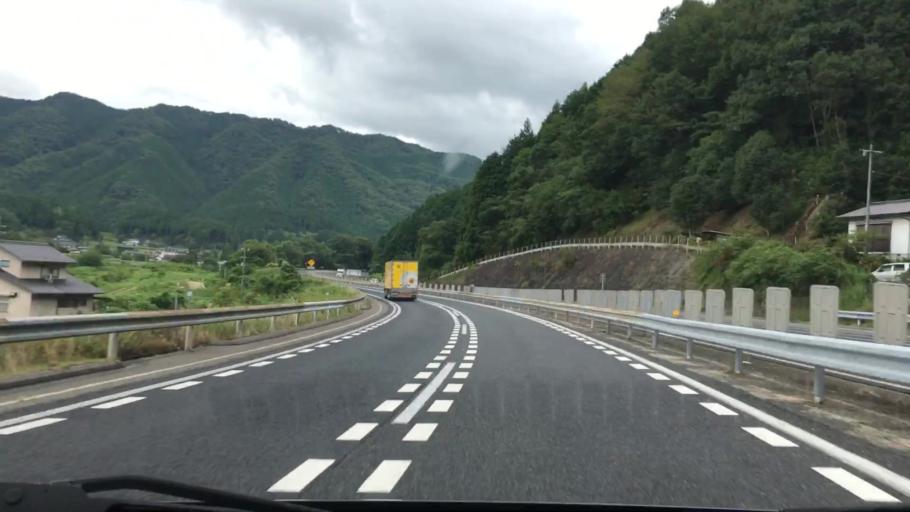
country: JP
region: Okayama
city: Takahashi
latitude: 34.9882
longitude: 133.7144
